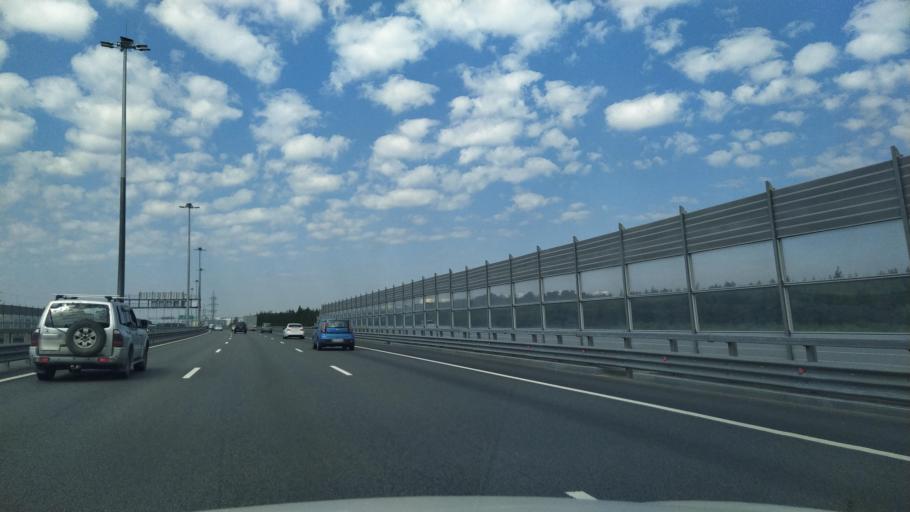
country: RU
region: St.-Petersburg
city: Pargolovo
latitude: 60.0986
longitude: 30.2955
